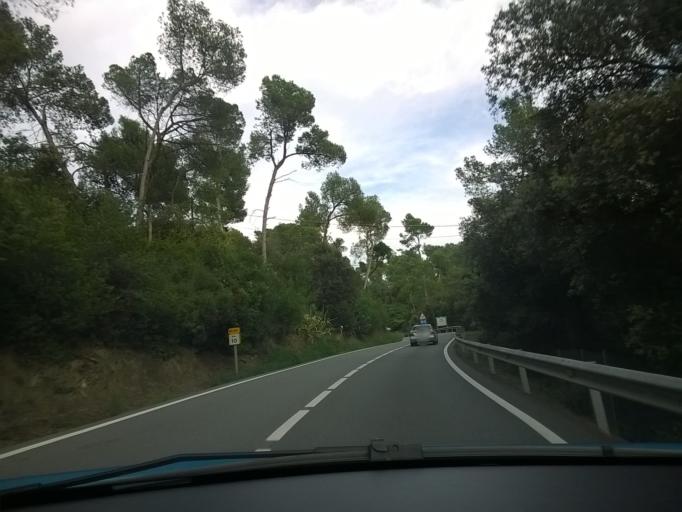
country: ES
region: Catalonia
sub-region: Provincia de Barcelona
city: Sant Cugat del Valles
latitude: 41.4532
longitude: 2.0905
